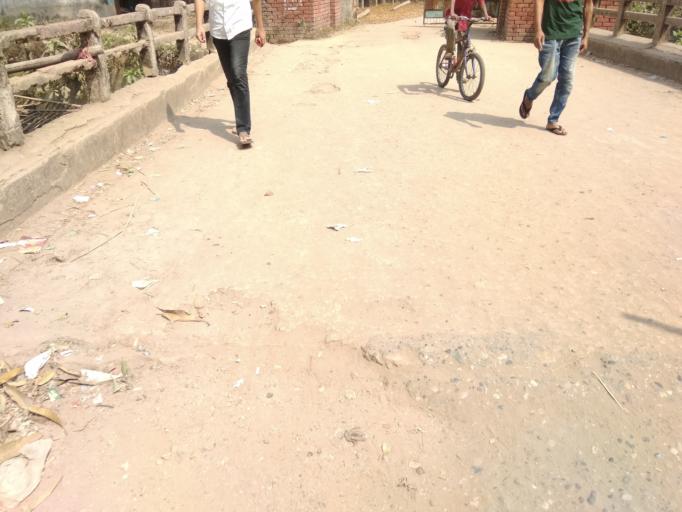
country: BD
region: Chittagong
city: Chittagong
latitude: 22.3683
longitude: 91.8213
